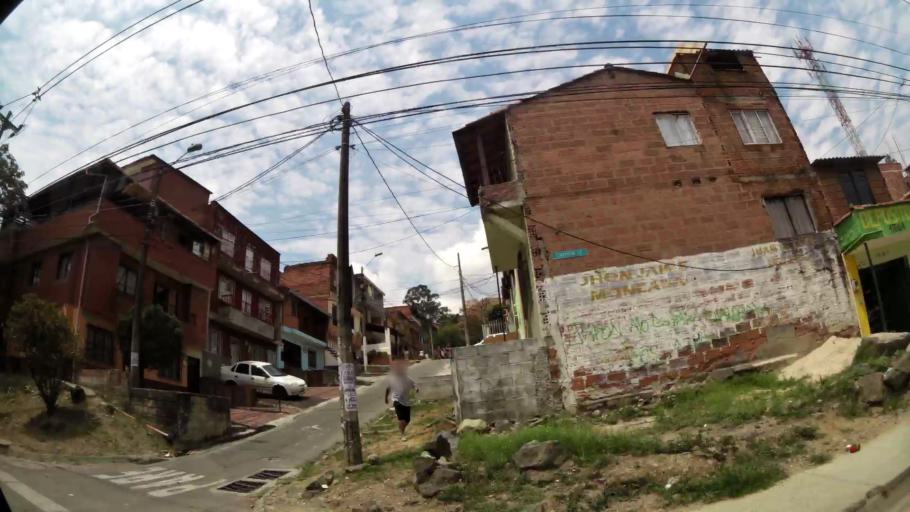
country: CO
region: Antioquia
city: Bello
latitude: 6.3054
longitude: -75.5712
